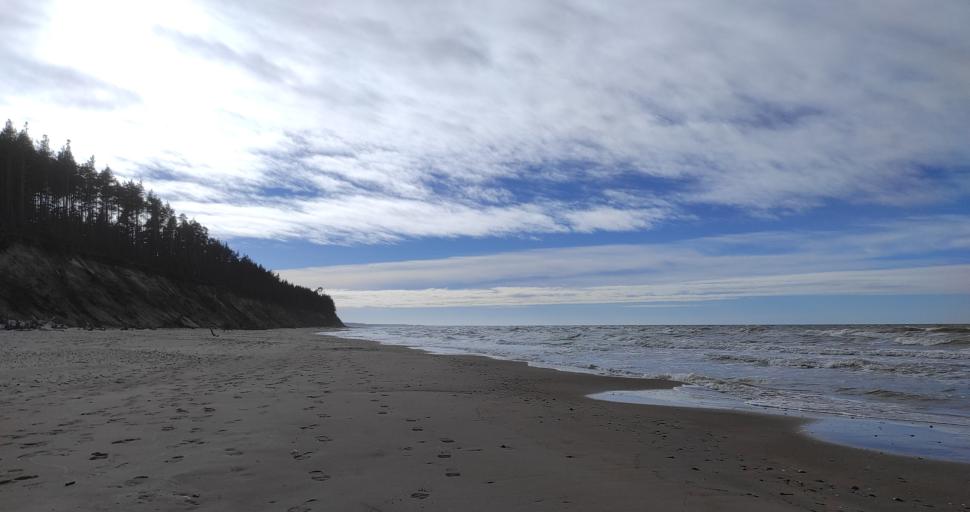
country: LV
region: Alsunga
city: Alsunga
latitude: 57.0251
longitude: 21.3930
